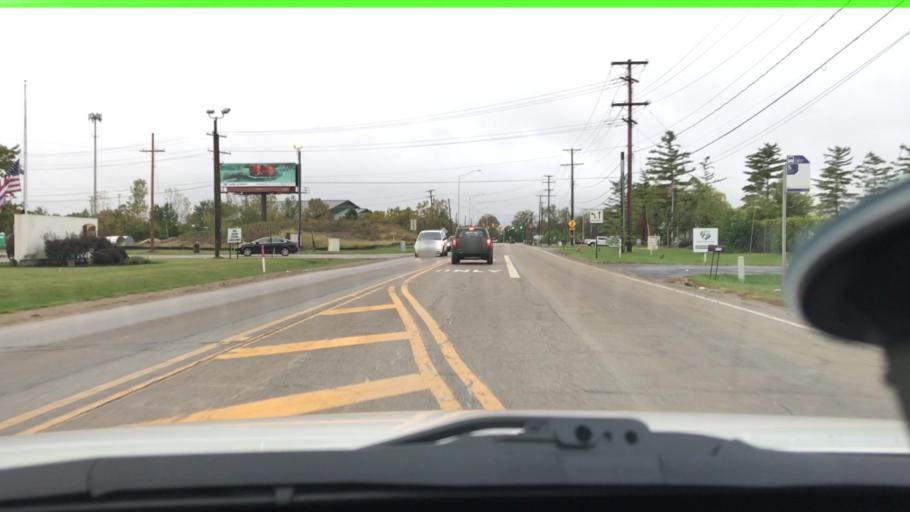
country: US
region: Ohio
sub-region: Franklin County
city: Lincoln Village
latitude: 39.9825
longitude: -83.1347
